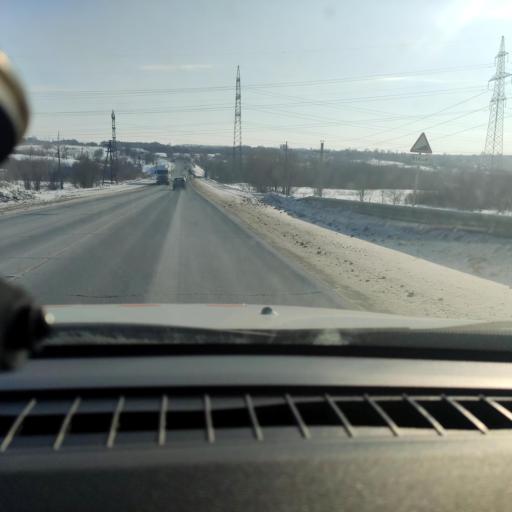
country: RU
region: Samara
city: Smyshlyayevka
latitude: 53.2829
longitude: 50.4615
